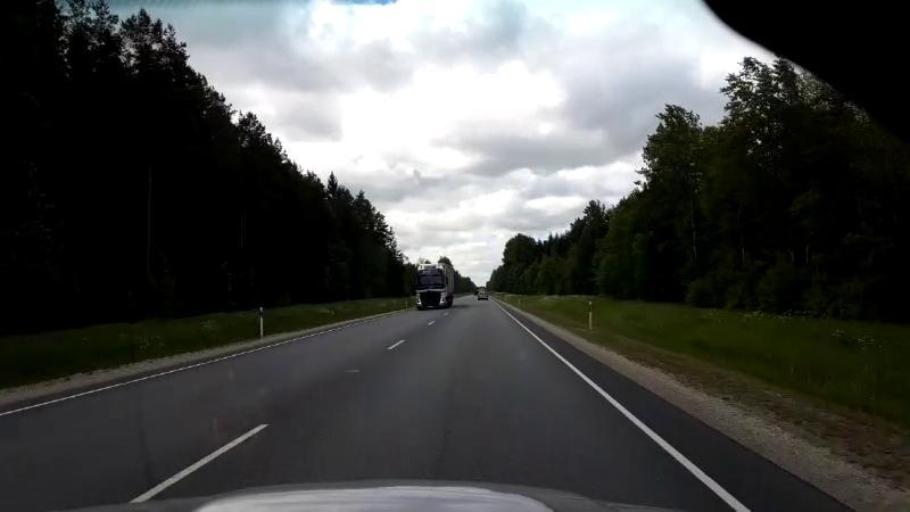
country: EE
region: Raplamaa
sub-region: Maerjamaa vald
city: Marjamaa
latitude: 58.7994
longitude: 24.4128
